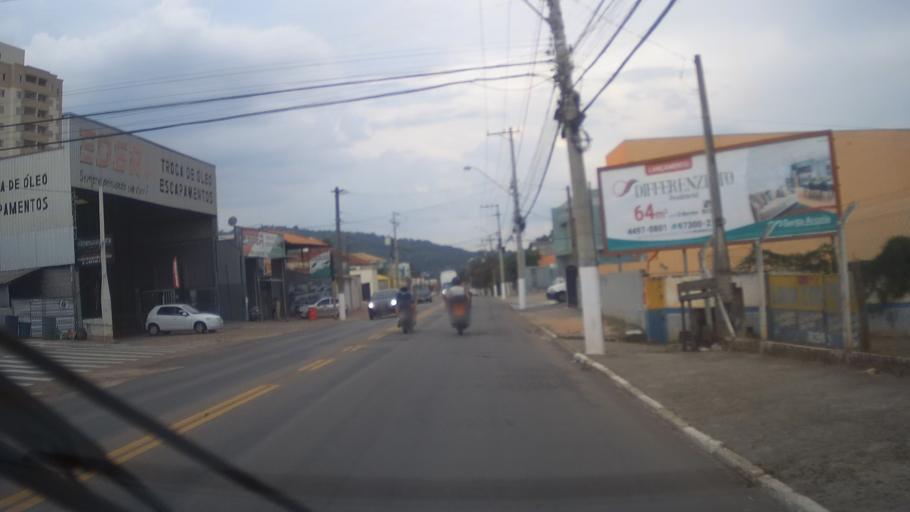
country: BR
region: Sao Paulo
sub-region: Itupeva
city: Itupeva
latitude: -23.1637
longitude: -47.0553
